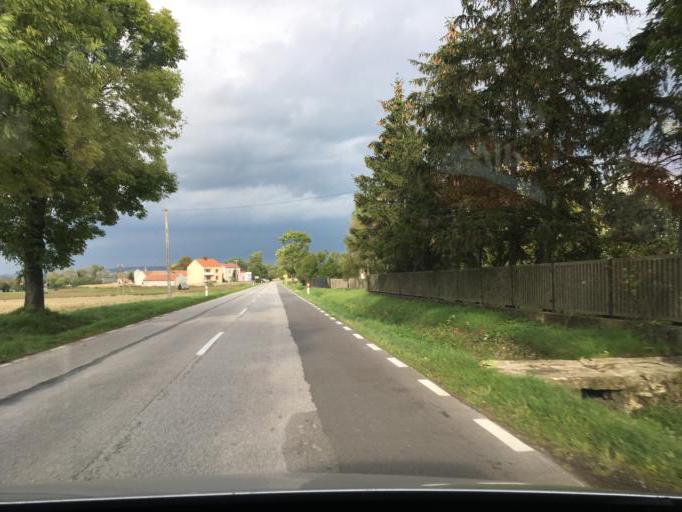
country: PL
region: Swietokrzyskie
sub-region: Powiat pinczowski
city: Michalow
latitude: 50.4848
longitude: 20.4507
